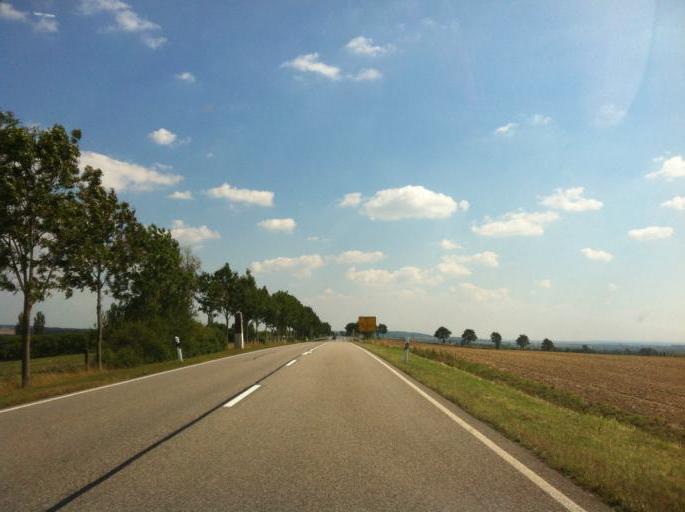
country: DE
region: Thuringia
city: Helmsdorf
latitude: 51.2700
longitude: 10.3946
